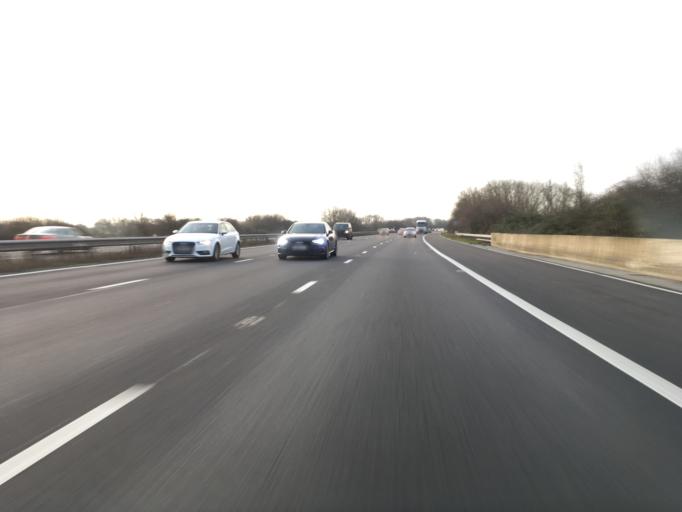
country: GB
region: England
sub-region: Gloucestershire
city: Uckington
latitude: 51.9442
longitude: -2.1264
